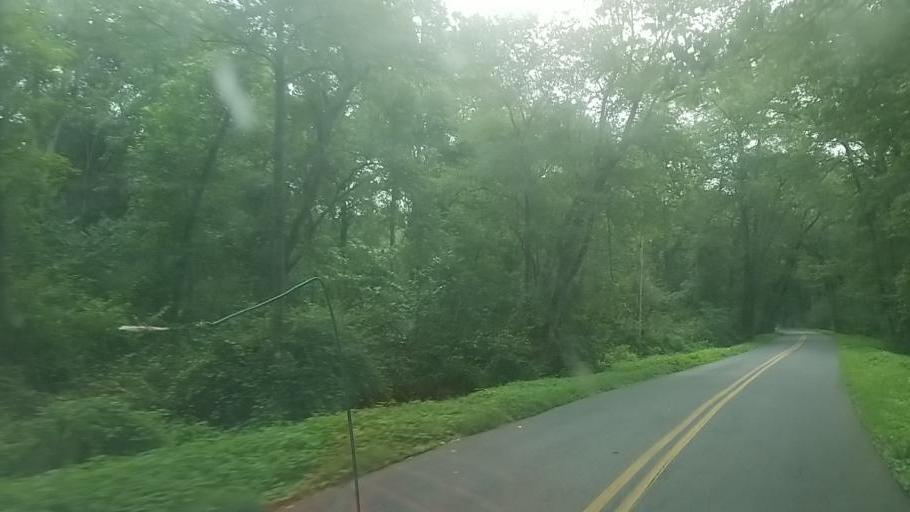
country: US
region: Maryland
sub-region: Wicomico County
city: Pittsville
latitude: 38.4410
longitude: -75.3342
